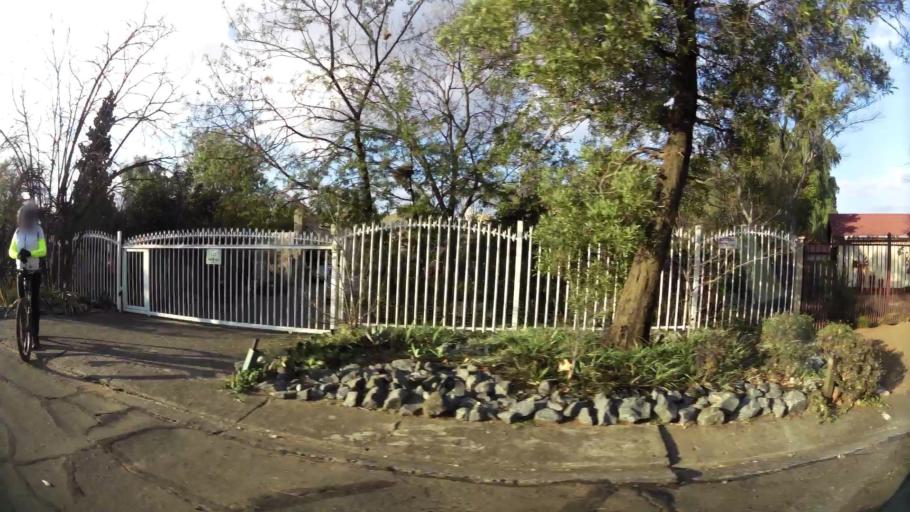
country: ZA
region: Orange Free State
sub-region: Mangaung Metropolitan Municipality
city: Bloemfontein
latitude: -29.1454
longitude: 26.1877
